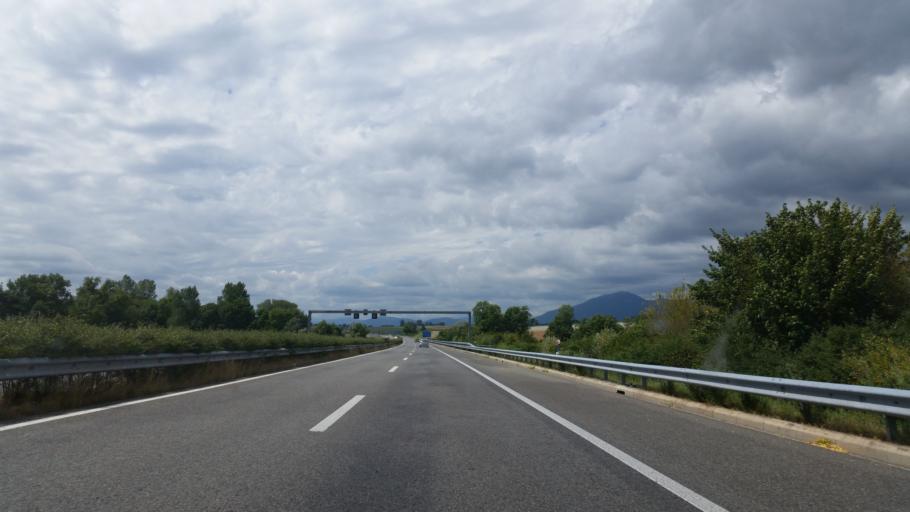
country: CH
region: Vaud
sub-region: Jura-Nord vaudois District
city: Grandson
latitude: 46.8316
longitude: 6.6736
